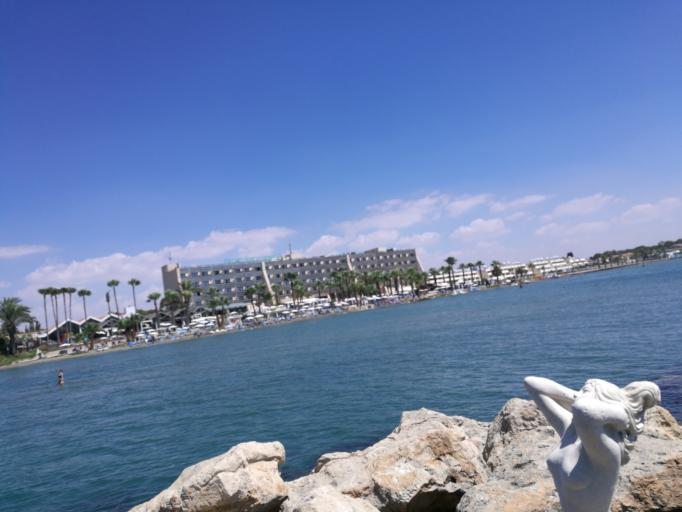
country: CY
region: Larnaka
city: Voroklini
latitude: 34.9684
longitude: 33.6731
